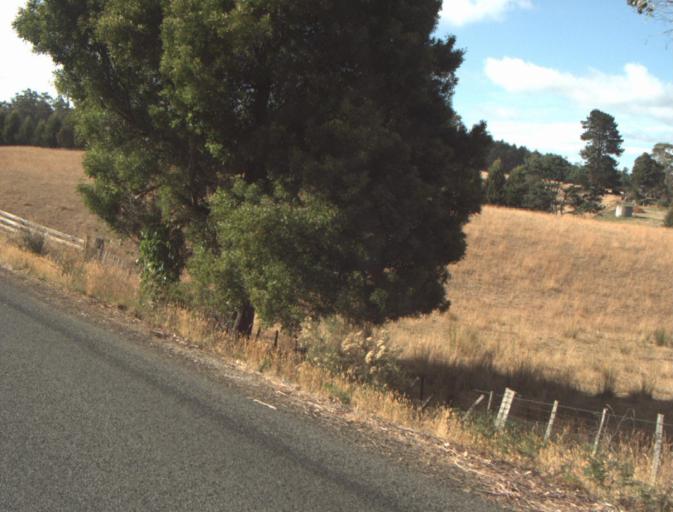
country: AU
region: Tasmania
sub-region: Dorset
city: Bridport
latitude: -41.1309
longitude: 147.2150
